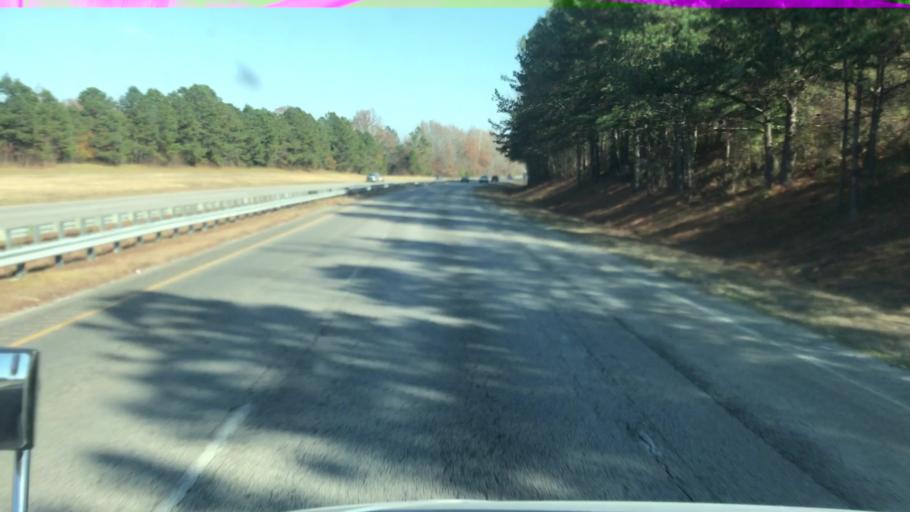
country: US
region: North Carolina
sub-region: Nash County
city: Nashville
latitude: 35.9751
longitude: -77.9324
